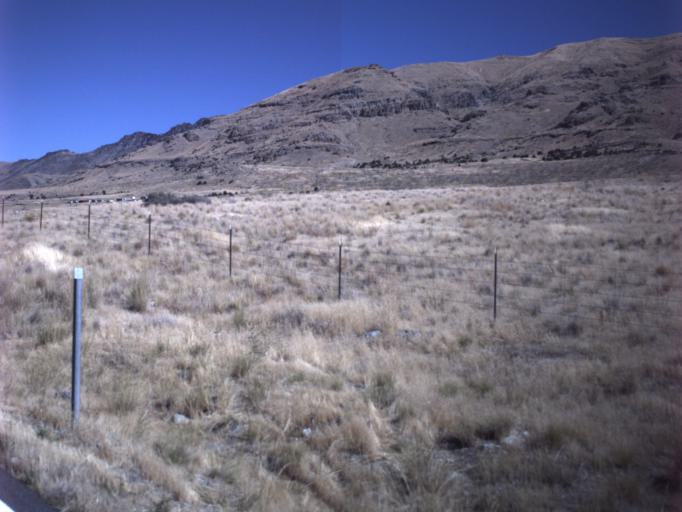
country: US
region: Utah
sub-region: Tooele County
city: Grantsville
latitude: 40.6707
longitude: -112.6739
